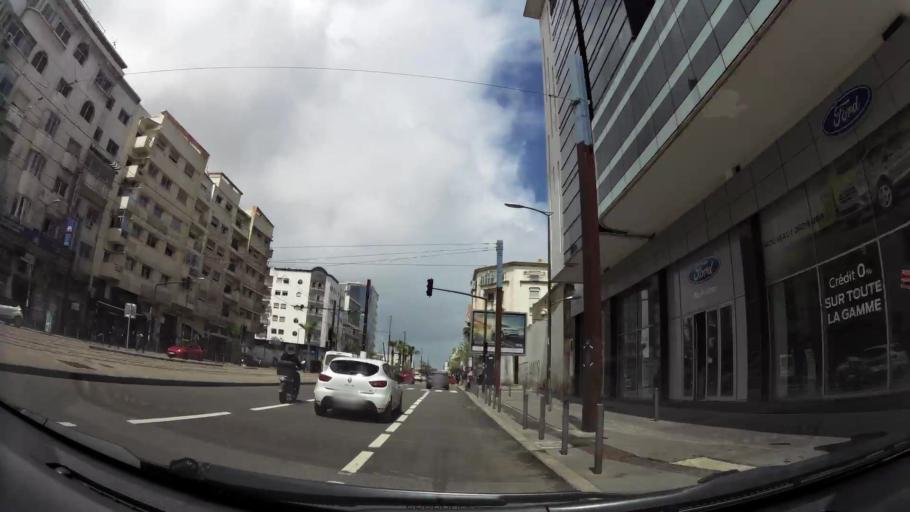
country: MA
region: Grand Casablanca
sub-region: Casablanca
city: Casablanca
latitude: 33.5698
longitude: -7.6258
